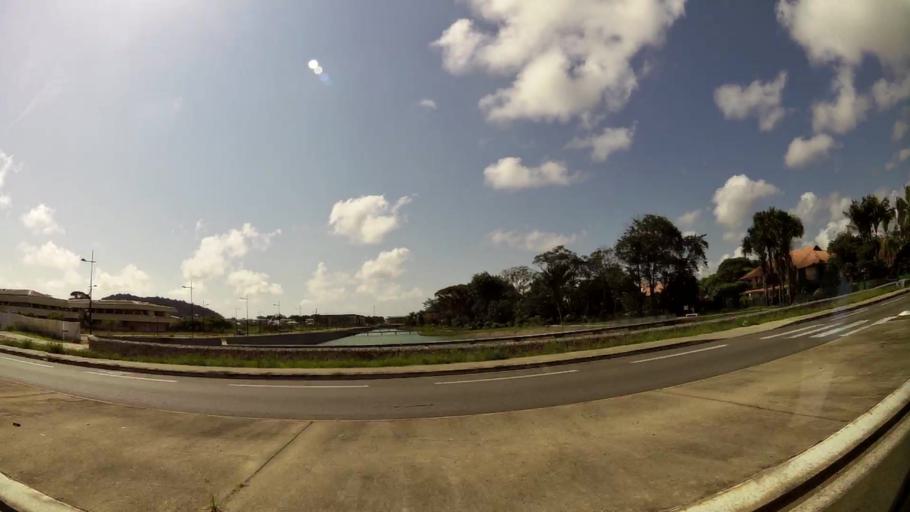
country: GF
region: Guyane
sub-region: Guyane
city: Cayenne
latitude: 4.9377
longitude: -52.3067
